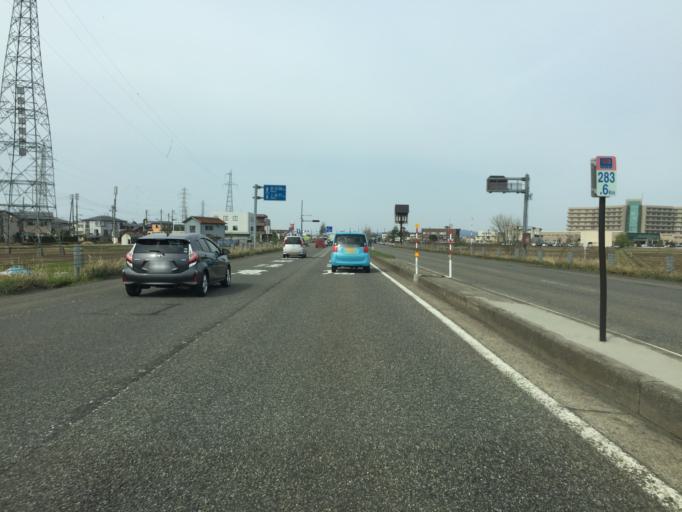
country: JP
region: Niigata
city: Nagaoka
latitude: 37.4476
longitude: 138.8732
